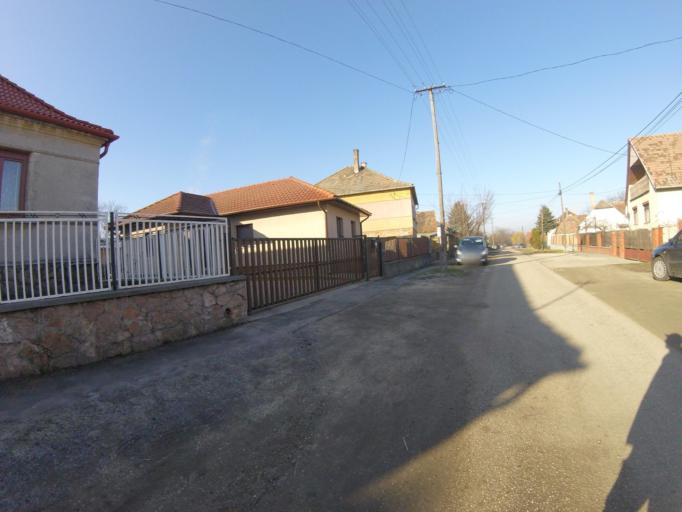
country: HU
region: Komarom-Esztergom
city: Bokod
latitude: 47.5209
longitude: 18.2186
